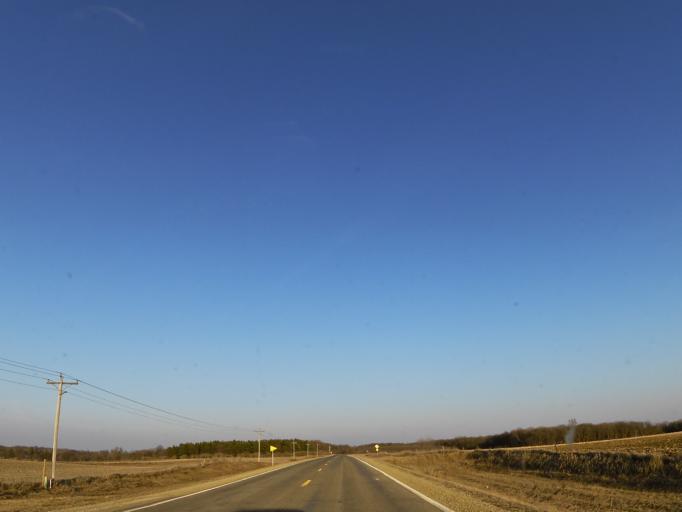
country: US
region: Iowa
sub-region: Mitchell County
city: Saint Ansgar
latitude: 43.3928
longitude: -92.9506
